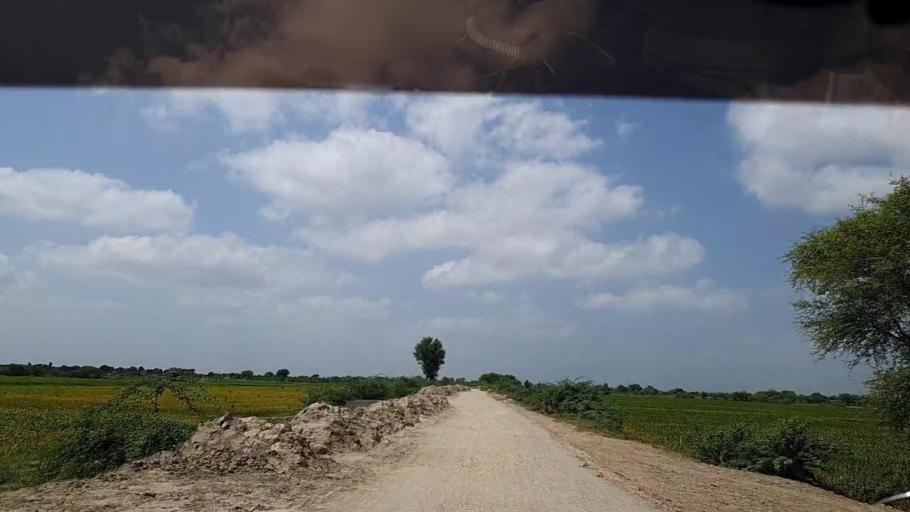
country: PK
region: Sindh
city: Badin
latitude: 24.5977
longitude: 68.7831
